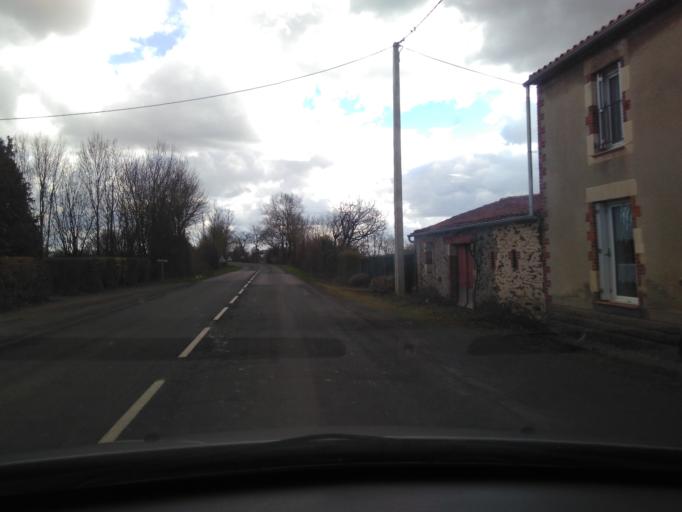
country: FR
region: Pays de la Loire
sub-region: Departement de la Vendee
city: Saint-Martin-des-Noyers
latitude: 46.7404
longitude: -1.1864
